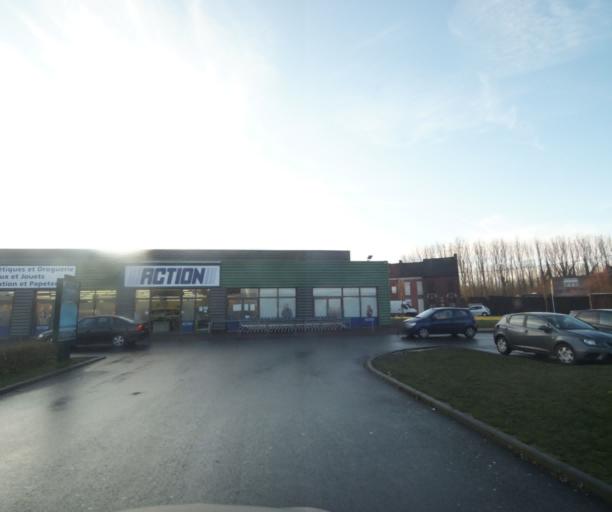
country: FR
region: Nord-Pas-de-Calais
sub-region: Departement du Nord
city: Quievrechain
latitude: 50.4000
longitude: 3.6600
